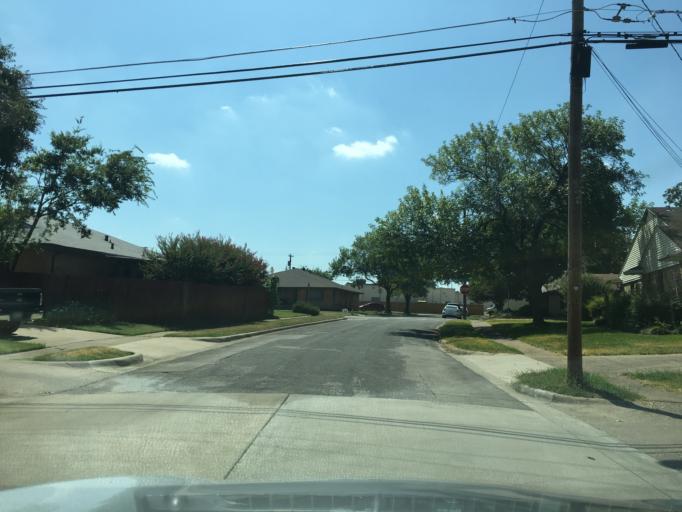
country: US
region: Texas
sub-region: Dallas County
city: Garland
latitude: 32.8525
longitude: -96.6871
